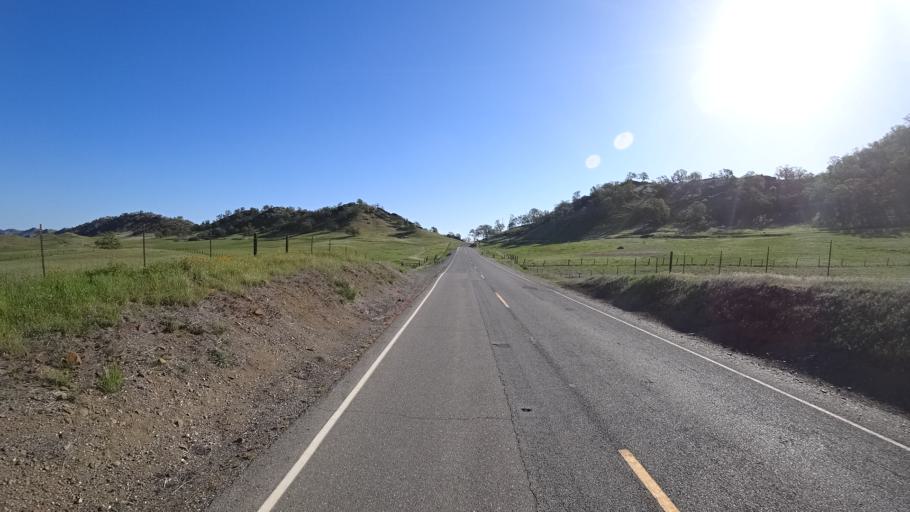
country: US
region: California
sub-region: Tehama County
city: Rancho Tehama Reserve
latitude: 39.7486
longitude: -122.5322
